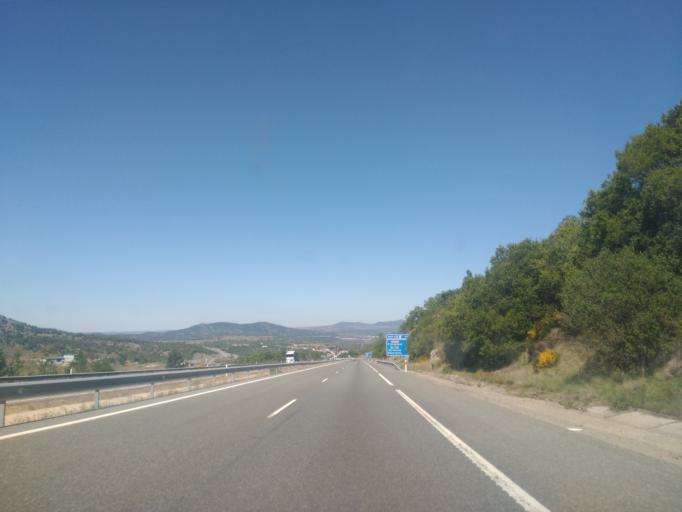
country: ES
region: Castille and Leon
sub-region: Provincia de Salamanca
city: Fresnedoso
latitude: 40.4255
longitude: -5.7031
